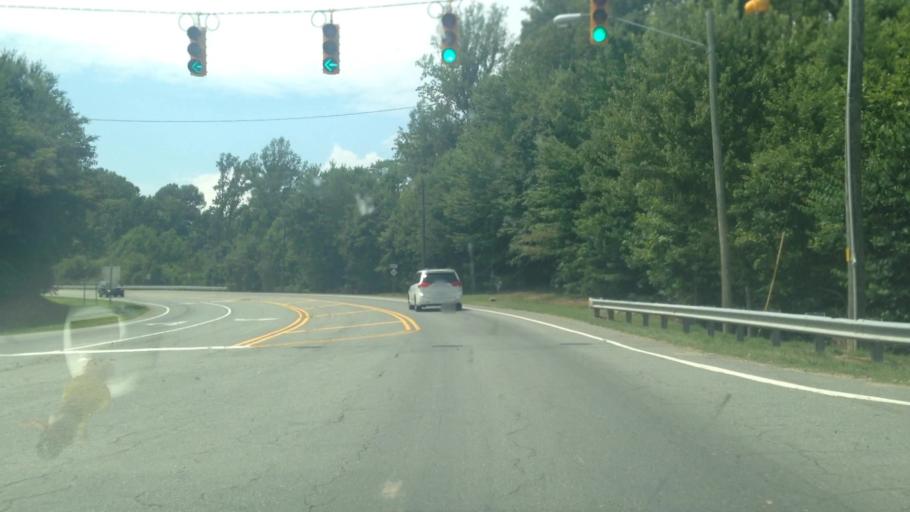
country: US
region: North Carolina
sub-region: Forsyth County
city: Walkertown
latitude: 36.1733
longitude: -80.1658
